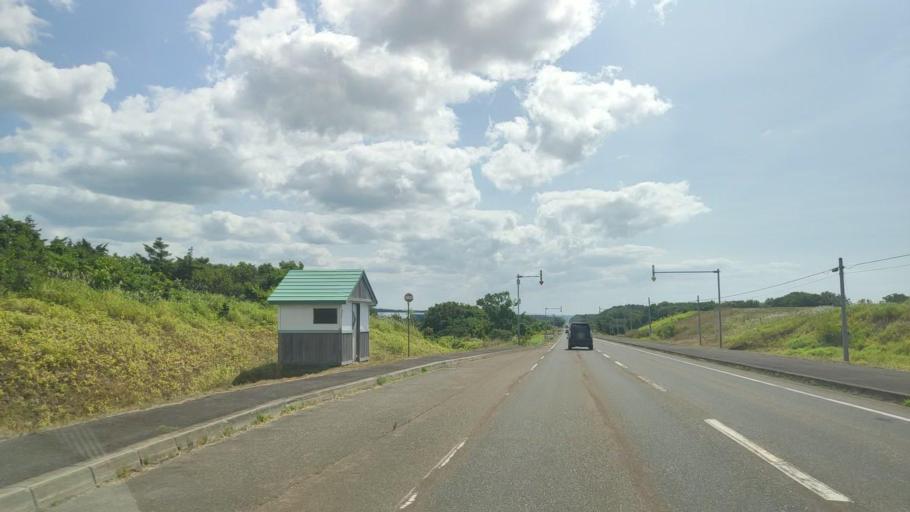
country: JP
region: Hokkaido
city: Makubetsu
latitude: 44.7849
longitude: 141.7903
